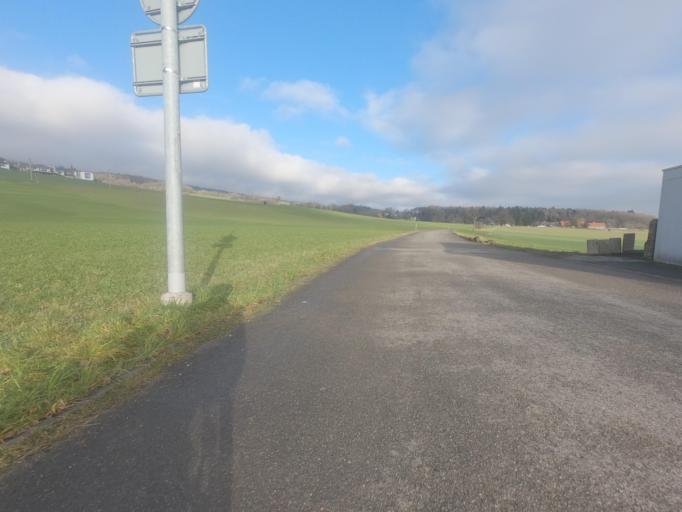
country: CH
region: Solothurn
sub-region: Bezirk Lebern
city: Bettlach
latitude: 47.2019
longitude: 7.4307
